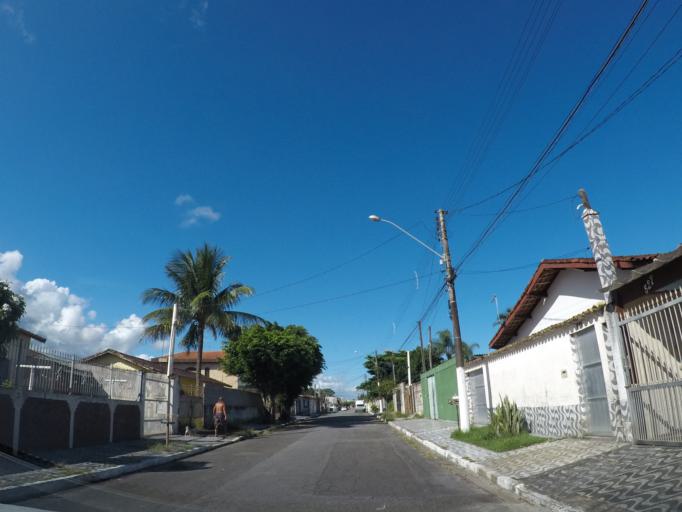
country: BR
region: Sao Paulo
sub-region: Mongagua
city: Mongagua
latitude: -24.0619
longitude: -46.5541
